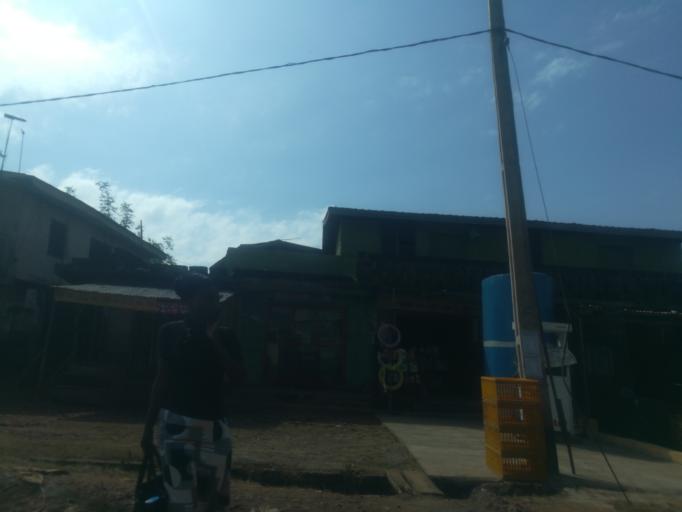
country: NG
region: Oyo
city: Ibadan
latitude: 7.4203
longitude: 3.9707
